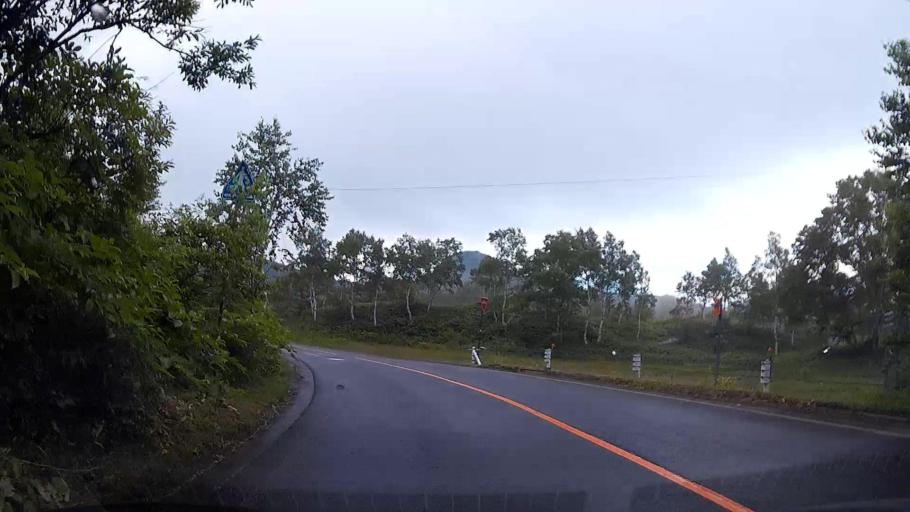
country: JP
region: Nagano
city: Nakano
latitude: 36.6967
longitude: 138.4916
